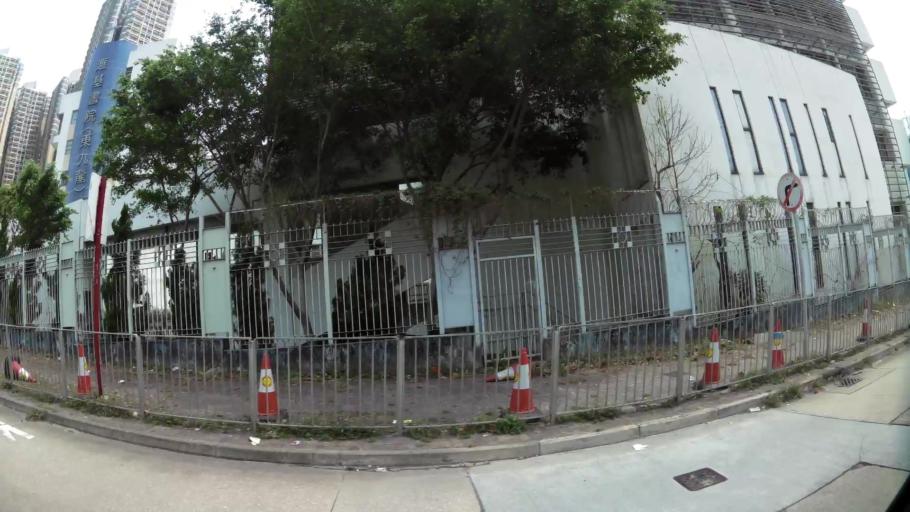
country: HK
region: Kowloon City
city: Kowloon
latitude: 22.3303
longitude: 114.2222
